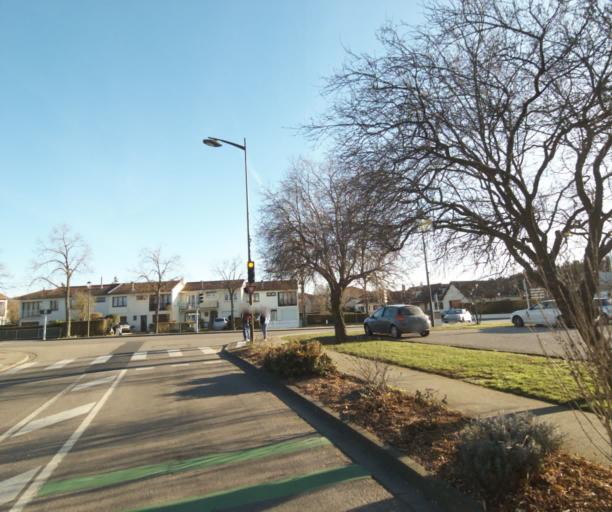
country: FR
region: Lorraine
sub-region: Departement de Meurthe-et-Moselle
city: Pulnoy
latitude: 48.7053
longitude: 6.2570
